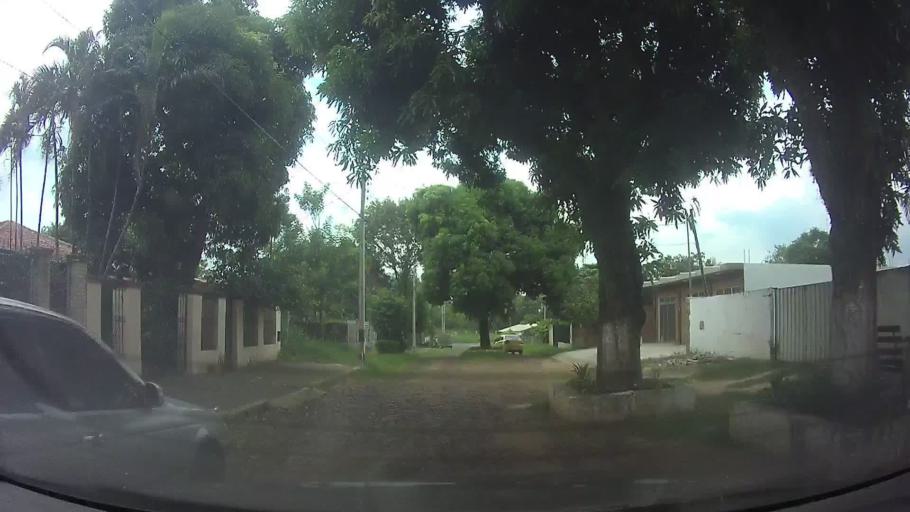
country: PY
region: Central
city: San Lorenzo
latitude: -25.2809
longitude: -57.4932
